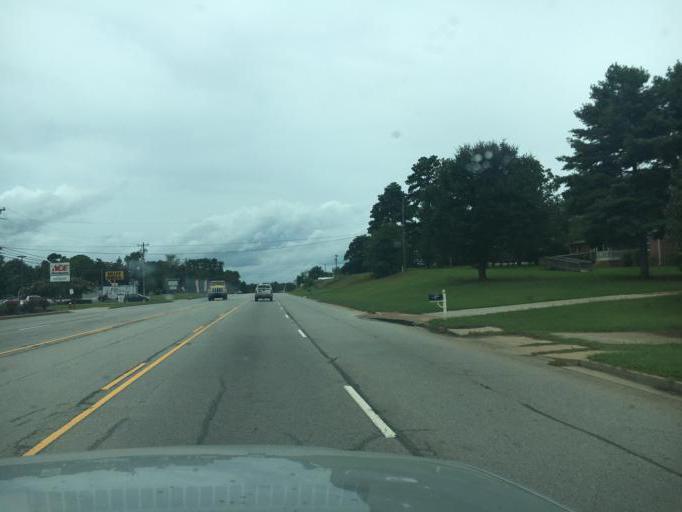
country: US
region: South Carolina
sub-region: Anderson County
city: Centerville
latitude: 34.5122
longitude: -82.7627
